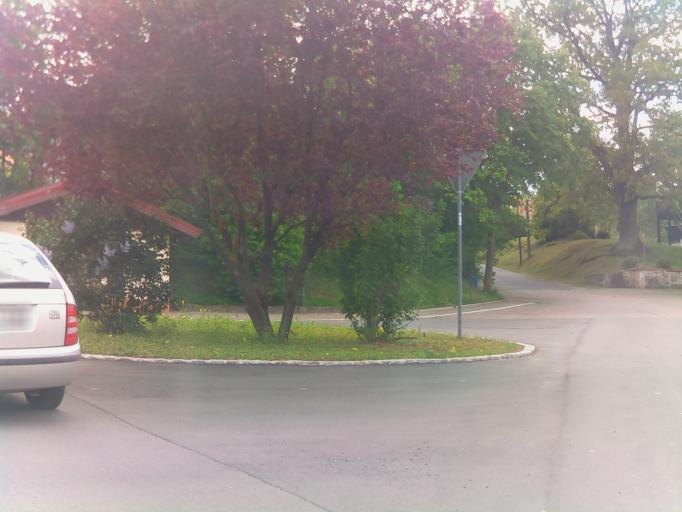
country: DE
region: Thuringia
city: Henneberg
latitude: 50.4975
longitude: 10.3909
